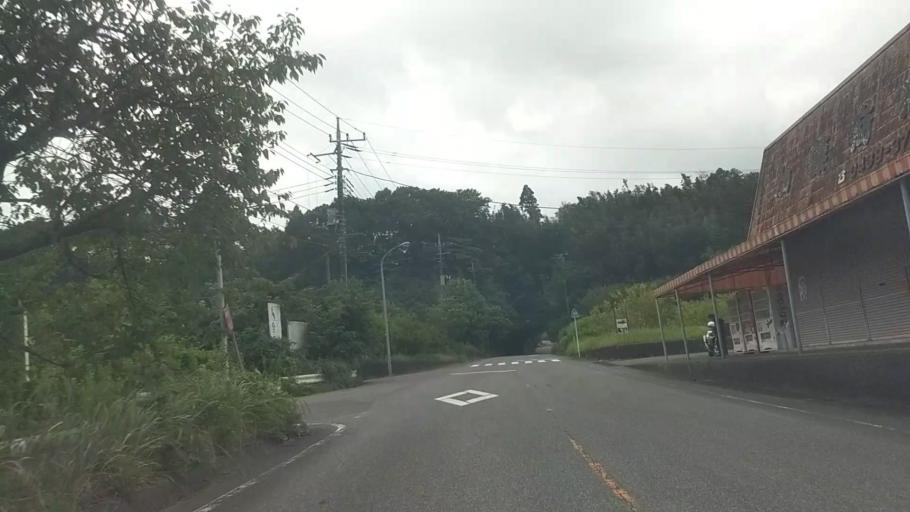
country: JP
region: Chiba
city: Kimitsu
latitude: 35.2514
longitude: 139.9961
